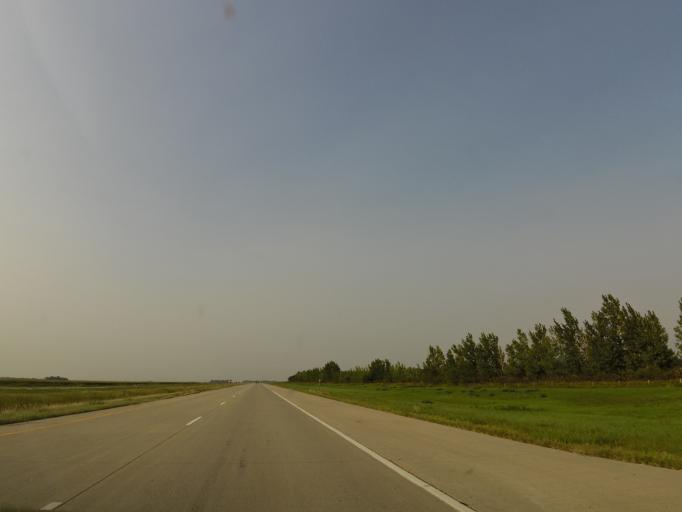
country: US
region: North Dakota
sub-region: Cass County
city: Horace
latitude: 46.5948
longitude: -96.8235
